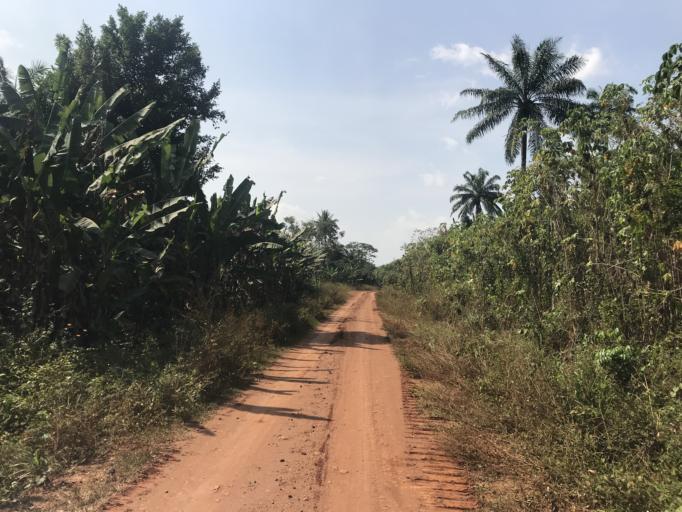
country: NG
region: Osun
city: Ilesa
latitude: 7.6304
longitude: 4.6824
